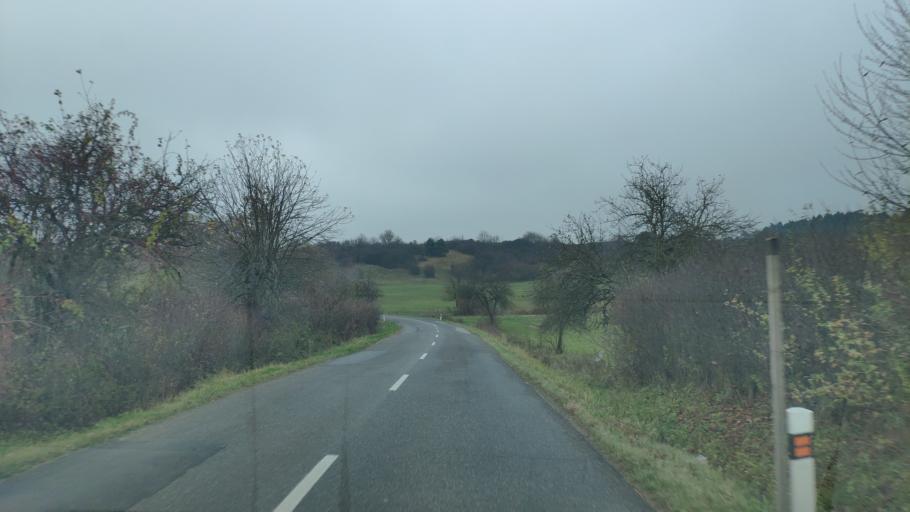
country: SK
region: Presovsky
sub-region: Okres Presov
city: Presov
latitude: 49.0892
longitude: 21.2142
